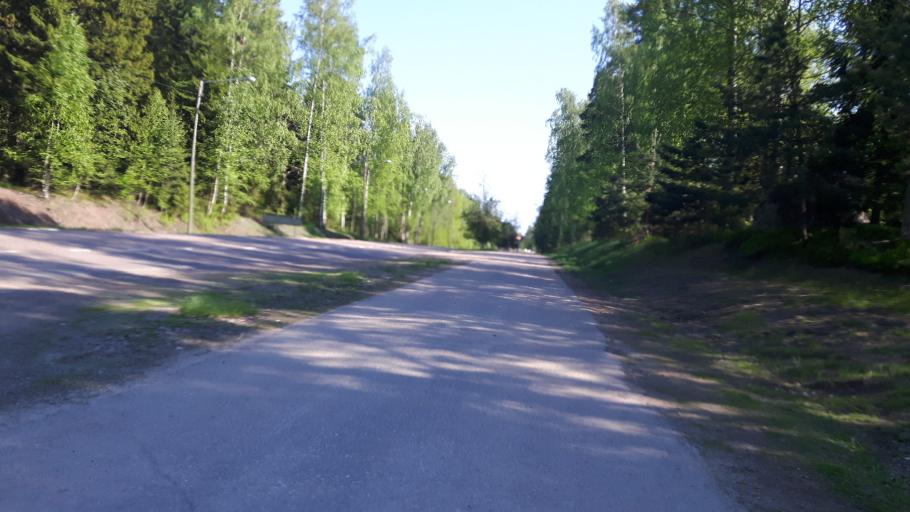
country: FI
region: Kymenlaakso
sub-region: Kotka-Hamina
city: Kotka
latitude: 60.4610
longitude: 26.8851
